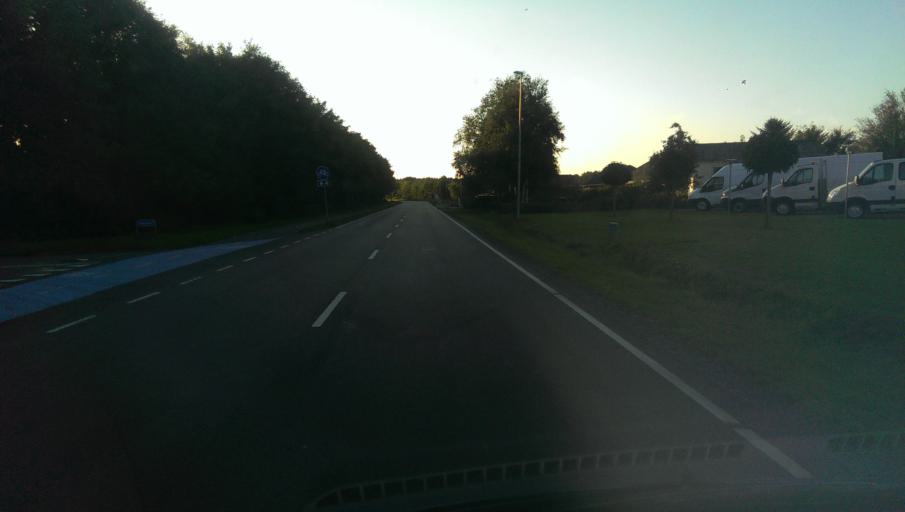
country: DK
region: South Denmark
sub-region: Esbjerg Kommune
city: Esbjerg
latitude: 55.5292
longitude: 8.4511
